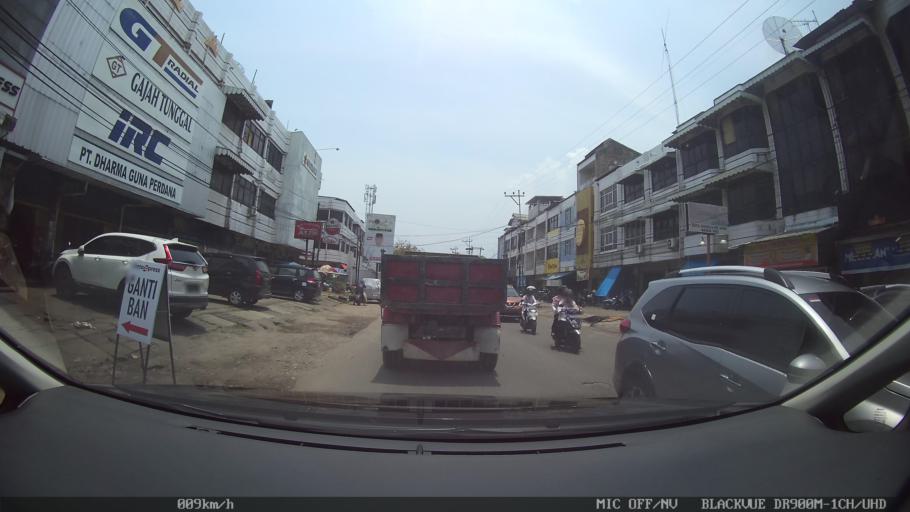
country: ID
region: Lampung
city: Bandarlampung
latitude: -5.4458
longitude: 105.2698
